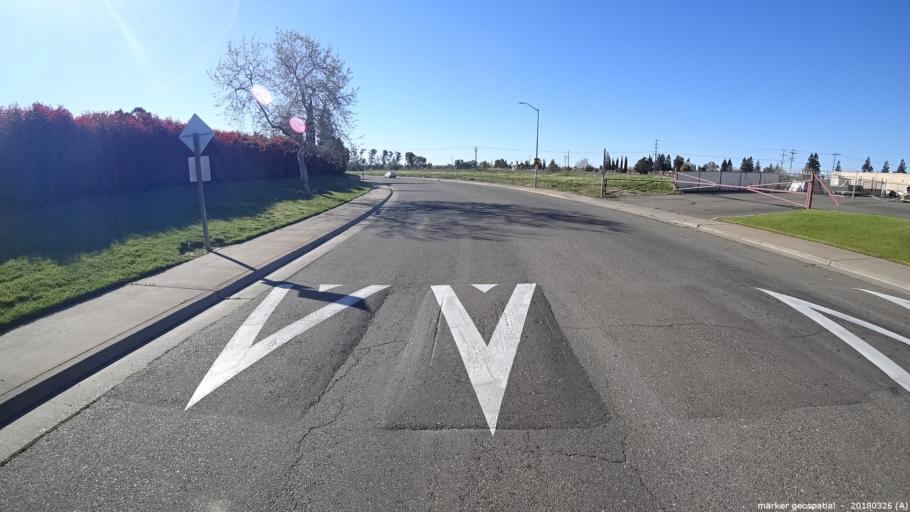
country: US
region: California
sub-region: Sacramento County
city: Florin
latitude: 38.4759
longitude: -121.3880
